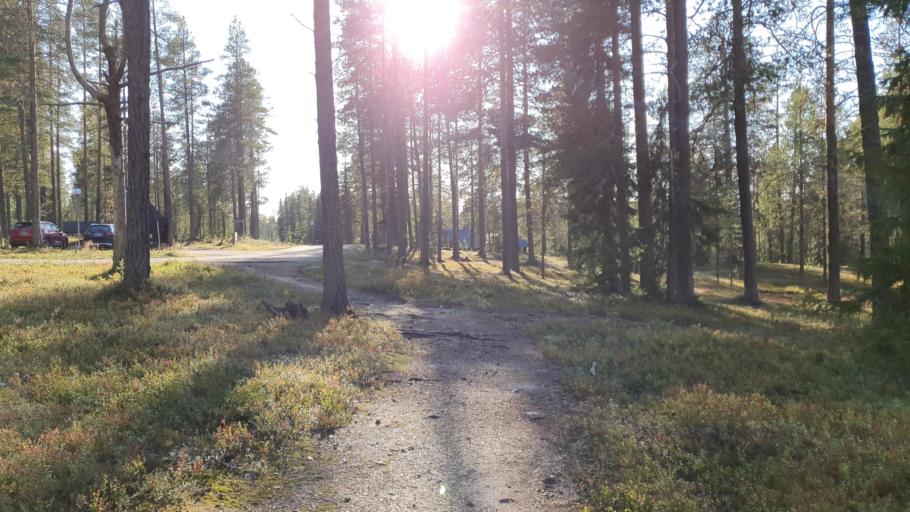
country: FI
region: Lapland
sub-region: Tunturi-Lappi
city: Kolari
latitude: 67.5997
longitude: 24.1884
